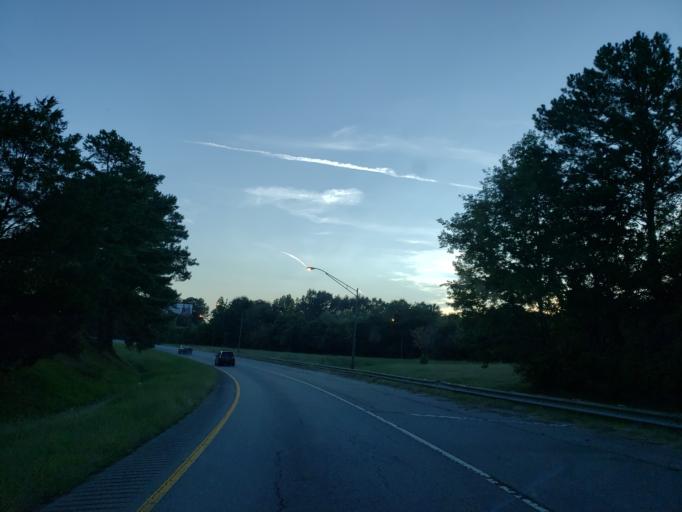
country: US
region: Georgia
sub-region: Floyd County
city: Rome
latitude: 34.2262
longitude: -85.1615
